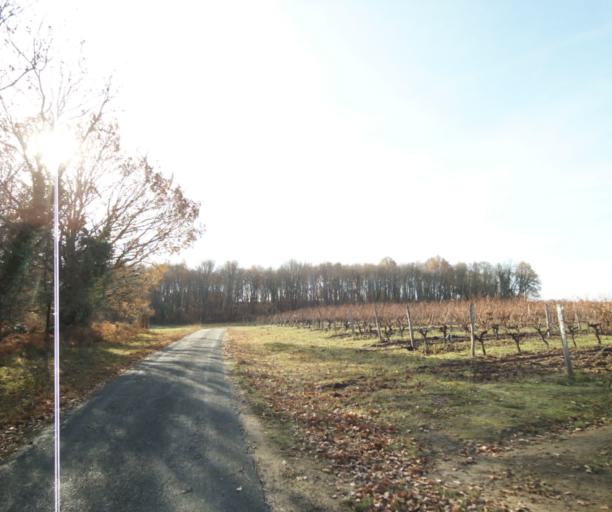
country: FR
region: Poitou-Charentes
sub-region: Departement de la Charente-Maritime
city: Burie
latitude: 45.7543
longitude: -0.4827
